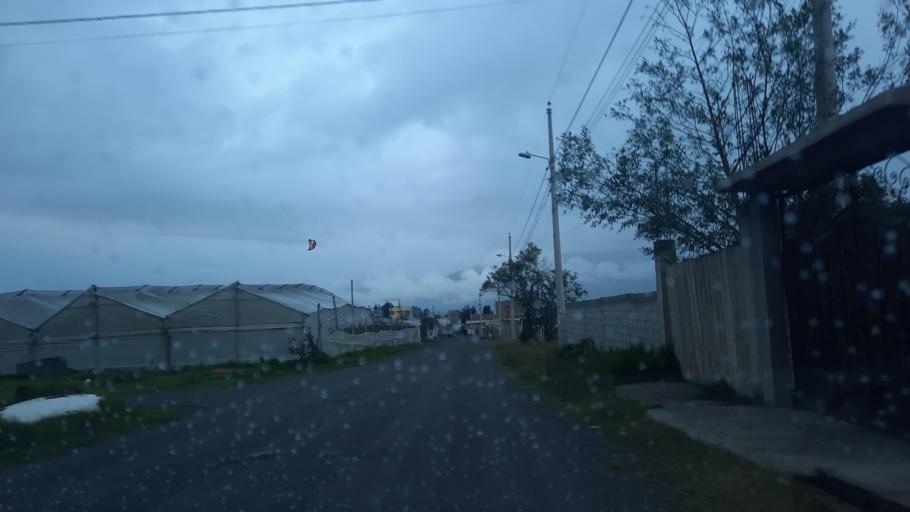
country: EC
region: Chimborazo
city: Riobamba
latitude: -1.6880
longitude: -78.6637
